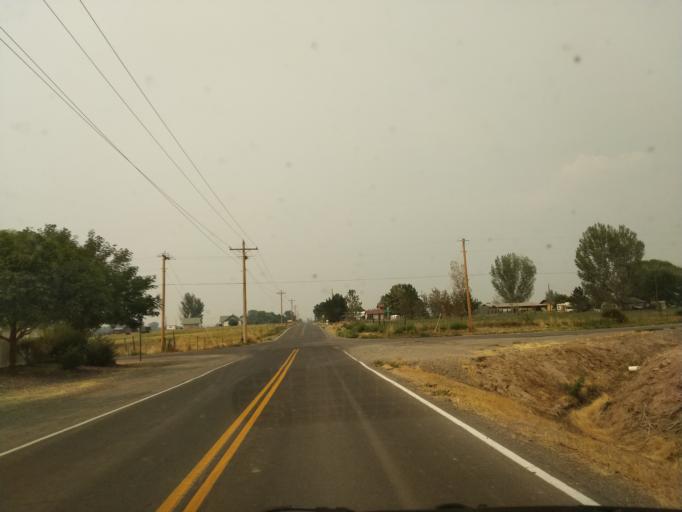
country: US
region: Colorado
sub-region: Mesa County
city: Fruitvale
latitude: 39.0334
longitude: -108.4967
